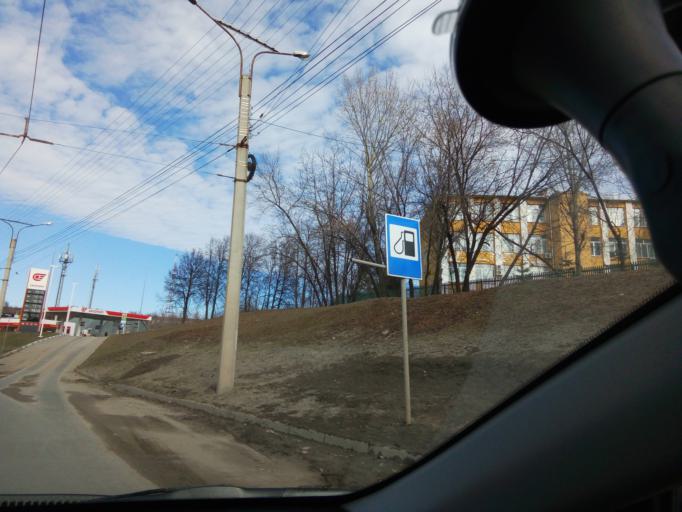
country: RU
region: Chuvashia
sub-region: Cheboksarskiy Rayon
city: Cheboksary
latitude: 56.1149
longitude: 47.2530
